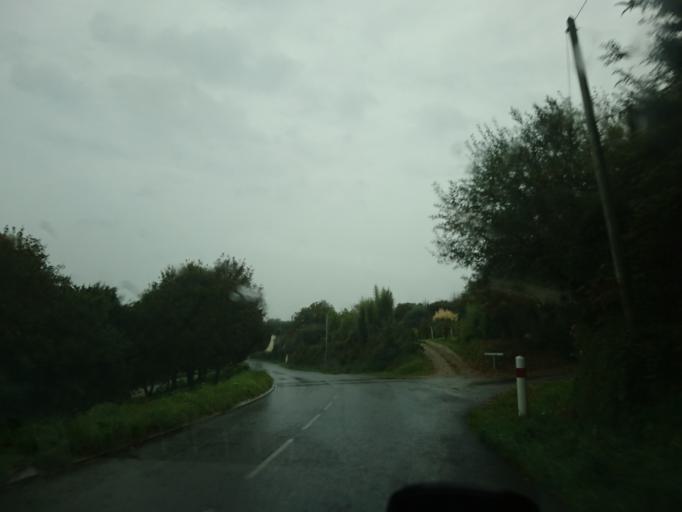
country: FR
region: Brittany
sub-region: Departement du Finistere
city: Plouguerneau
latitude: 48.5954
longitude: -4.5107
